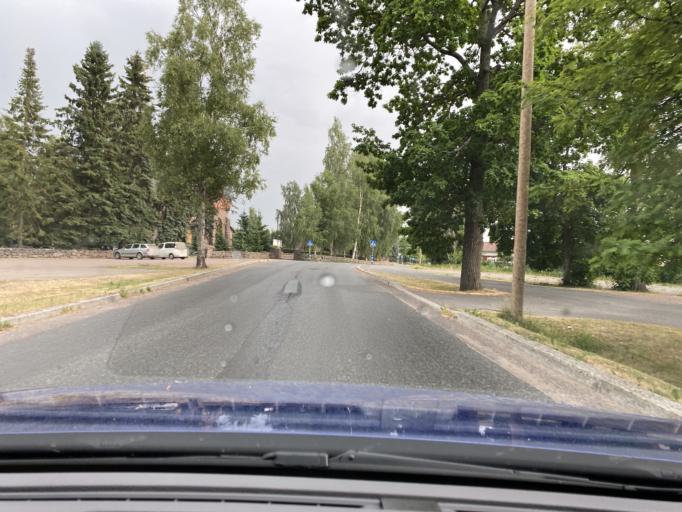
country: FI
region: Satakunta
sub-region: Rauma
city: Eura
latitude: 61.1339
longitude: 22.1289
